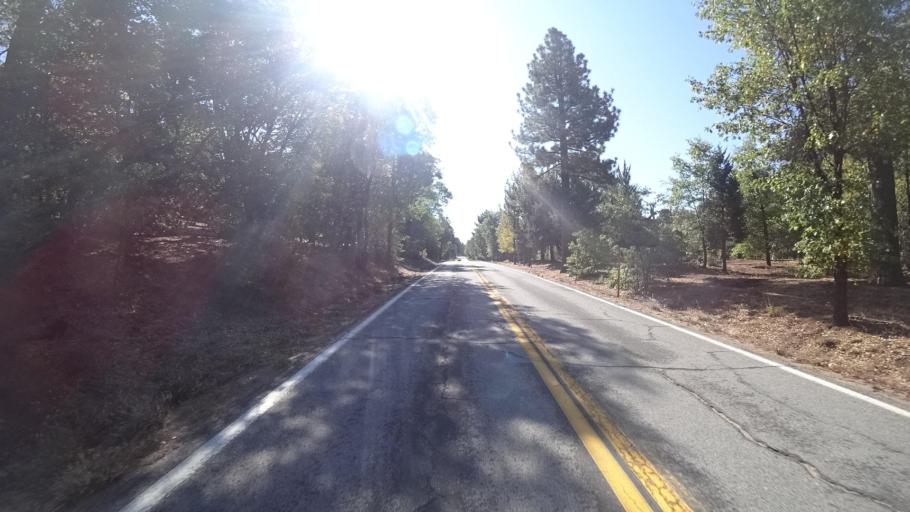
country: US
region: California
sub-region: San Diego County
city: Pine Valley
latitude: 32.8780
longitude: -116.4217
